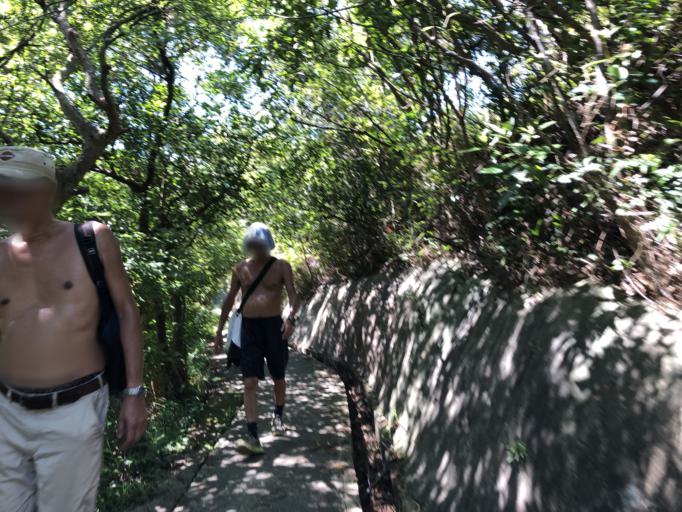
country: HK
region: Tuen Mun
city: Tuen Mun
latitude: 22.2836
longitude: 113.9834
